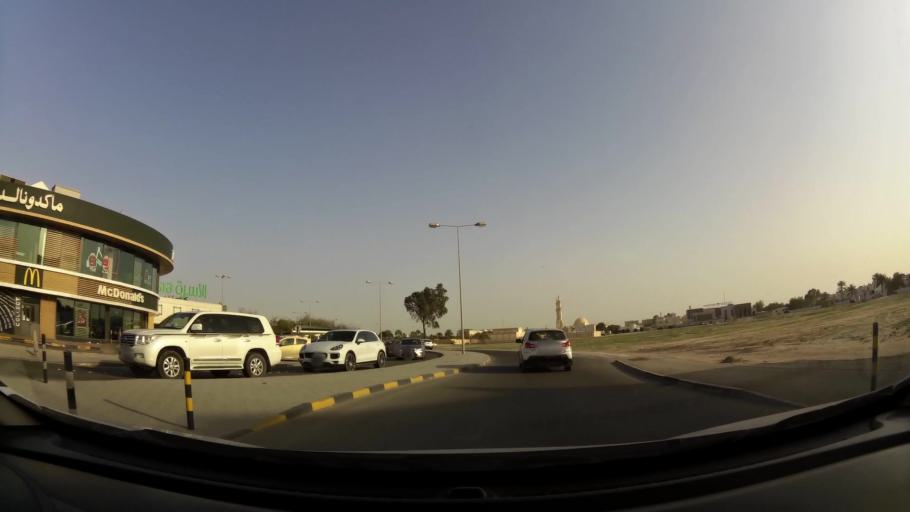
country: BH
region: Manama
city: Jidd Hafs
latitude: 26.2168
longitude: 50.4787
